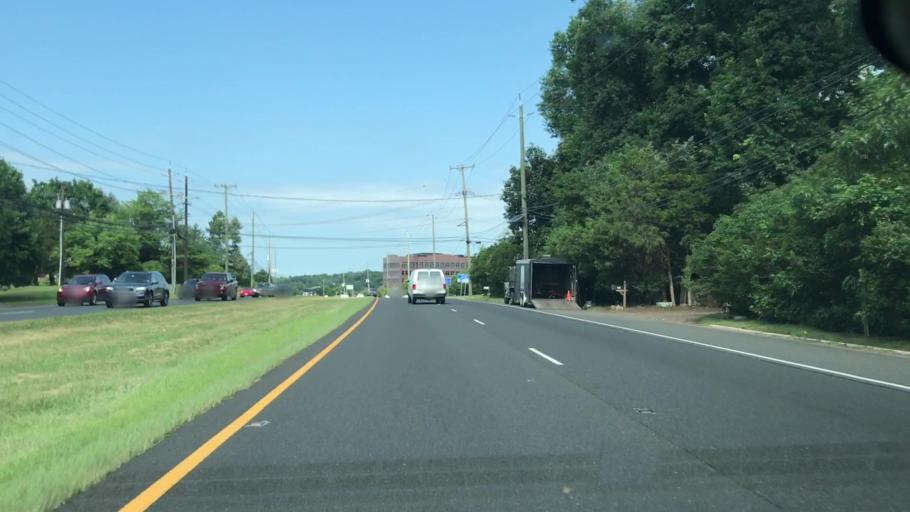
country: US
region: New Jersey
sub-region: Somerset County
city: Bradley Gardens
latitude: 40.5745
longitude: -74.6617
